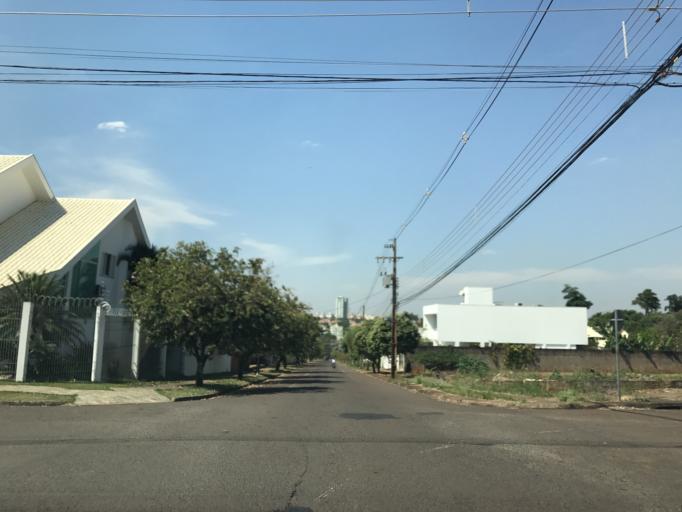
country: BR
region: Parana
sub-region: Maringa
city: Maringa
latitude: -23.4449
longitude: -51.9482
